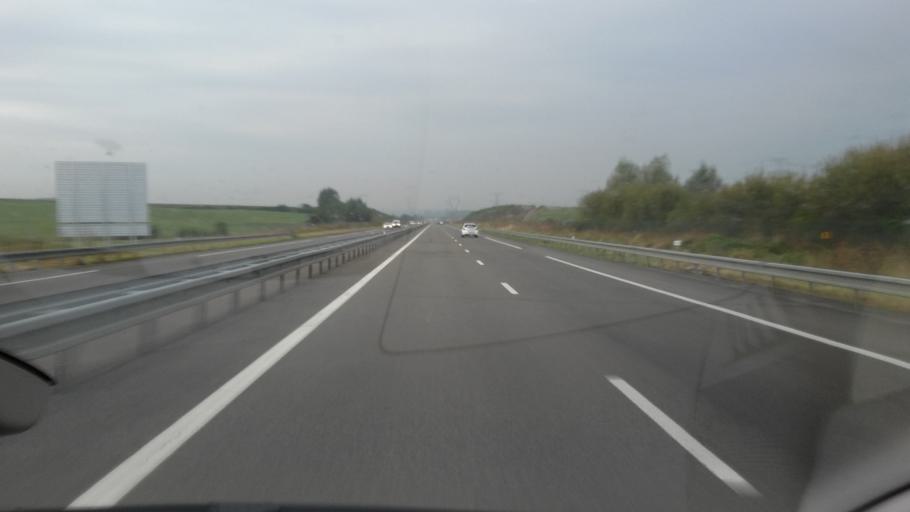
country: FR
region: Champagne-Ardenne
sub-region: Departement des Ardennes
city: Rethel
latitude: 49.5786
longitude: 4.4823
